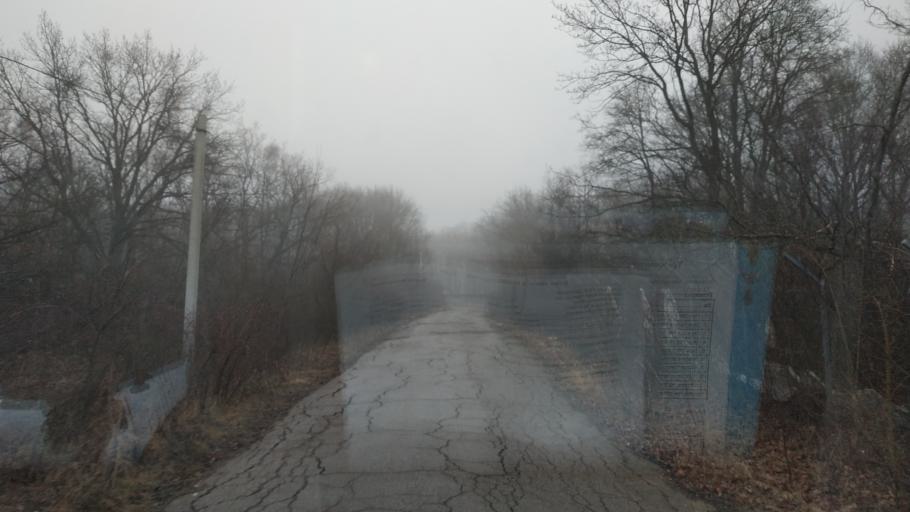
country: MD
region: Laloveni
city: Ialoveni
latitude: 46.9490
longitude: 28.6995
